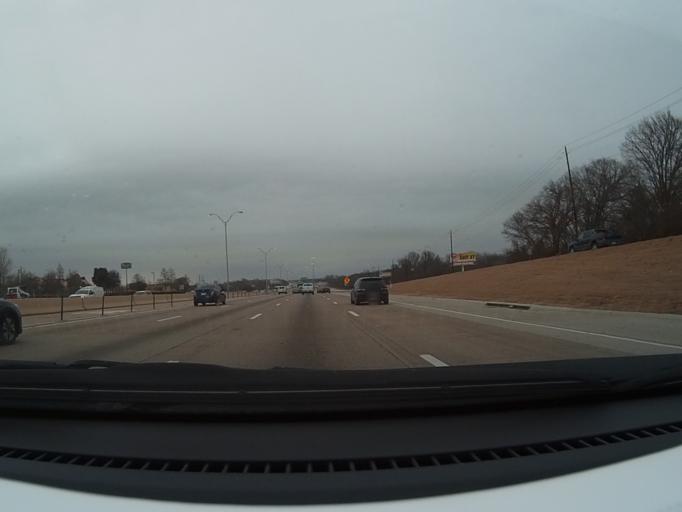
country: US
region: Texas
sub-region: Collin County
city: Allen
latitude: 33.0684
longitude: -96.6892
